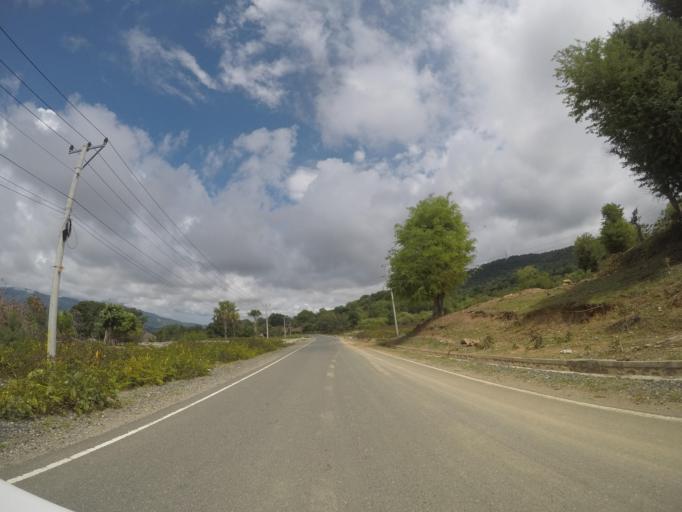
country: TL
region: Liquica
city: Maubara
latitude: -8.7462
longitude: 125.1079
